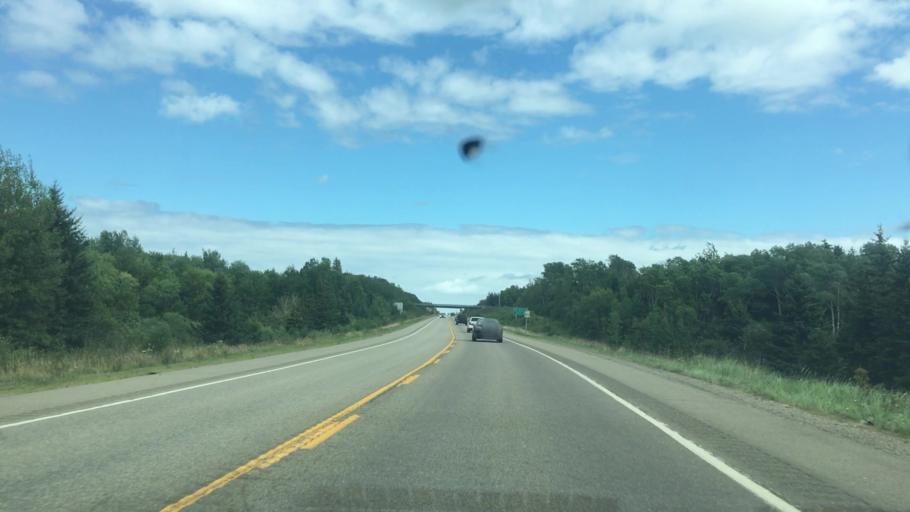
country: CA
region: Nova Scotia
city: Port Hawkesbury
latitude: 45.6169
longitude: -61.6191
